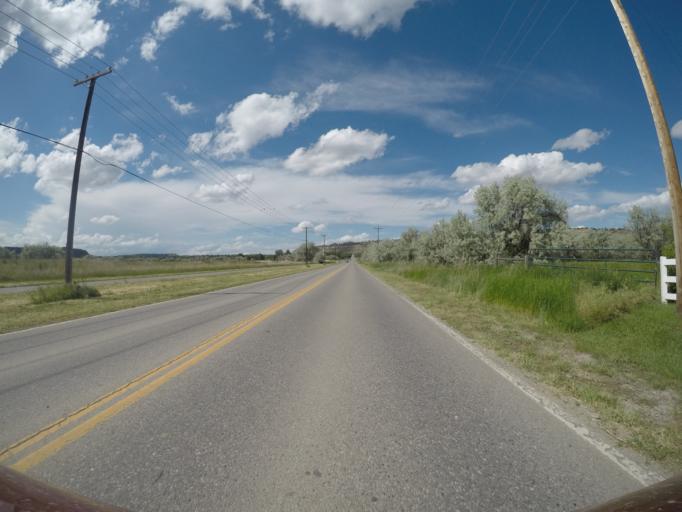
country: US
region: Montana
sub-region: Yellowstone County
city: Billings
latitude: 45.7930
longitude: -108.6527
